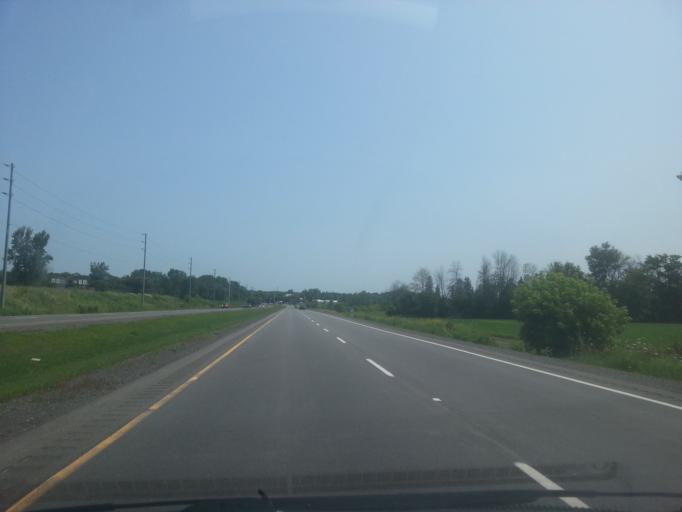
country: CA
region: Ontario
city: Ottawa
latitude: 45.4323
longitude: -75.5504
